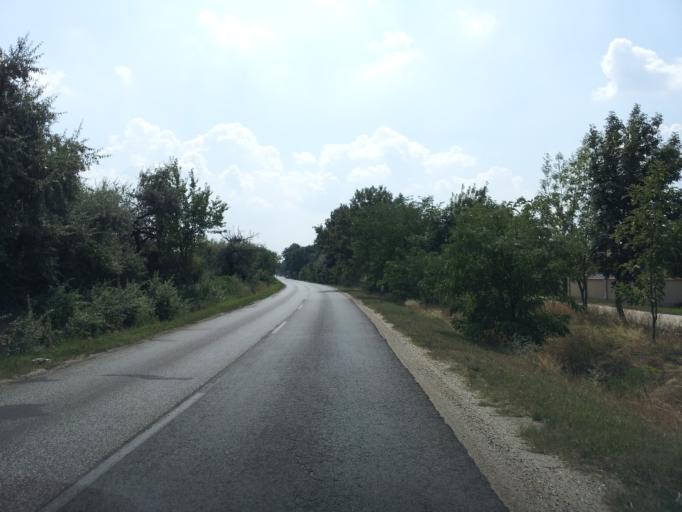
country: HU
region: Pest
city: Taksony
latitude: 47.3249
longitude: 19.0533
